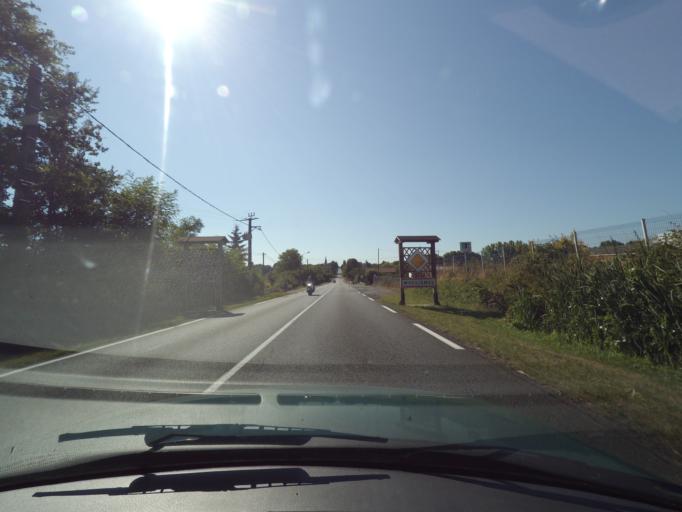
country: FR
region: Poitou-Charentes
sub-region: Departement de la Vienne
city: Saulge
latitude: 46.3354
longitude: 0.8059
